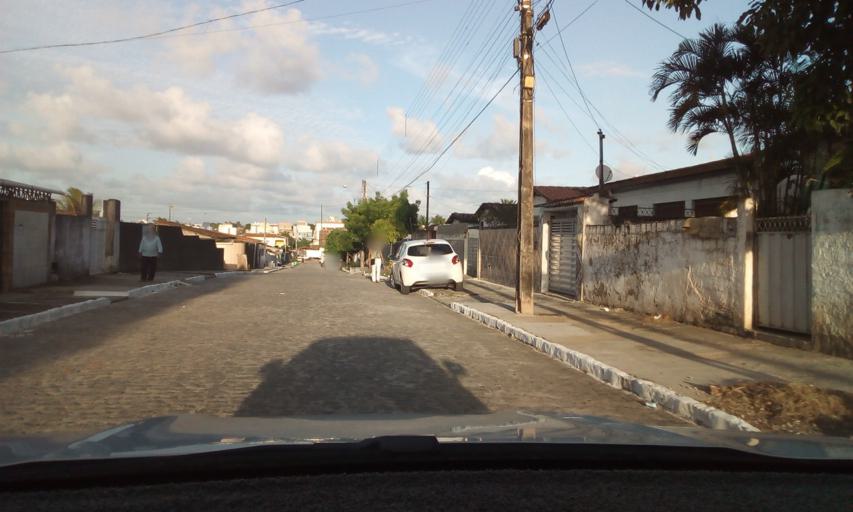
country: BR
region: Paraiba
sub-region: Bayeux
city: Bayeux
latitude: -7.1737
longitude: -34.8906
